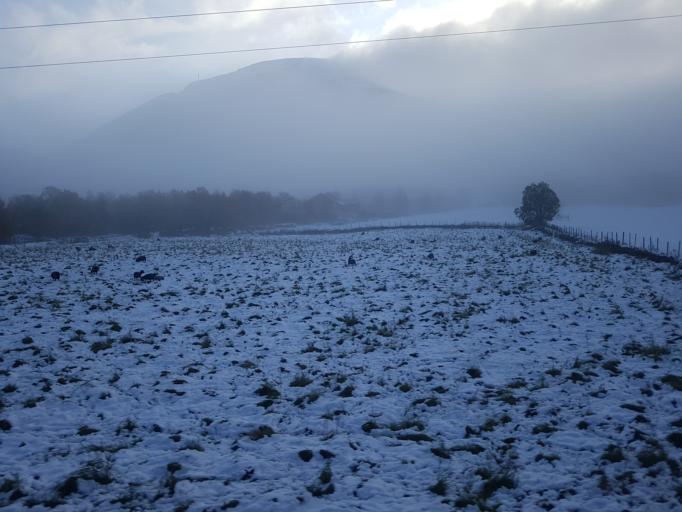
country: NO
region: Sor-Trondelag
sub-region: Oppdal
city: Oppdal
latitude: 62.5724
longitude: 9.6488
